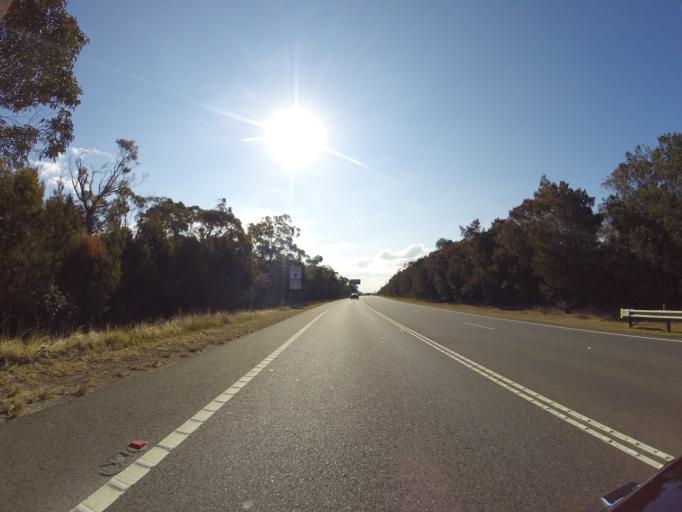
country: AU
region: New South Wales
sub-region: Sutherland Shire
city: Engadine
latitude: -34.0480
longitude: 150.9619
